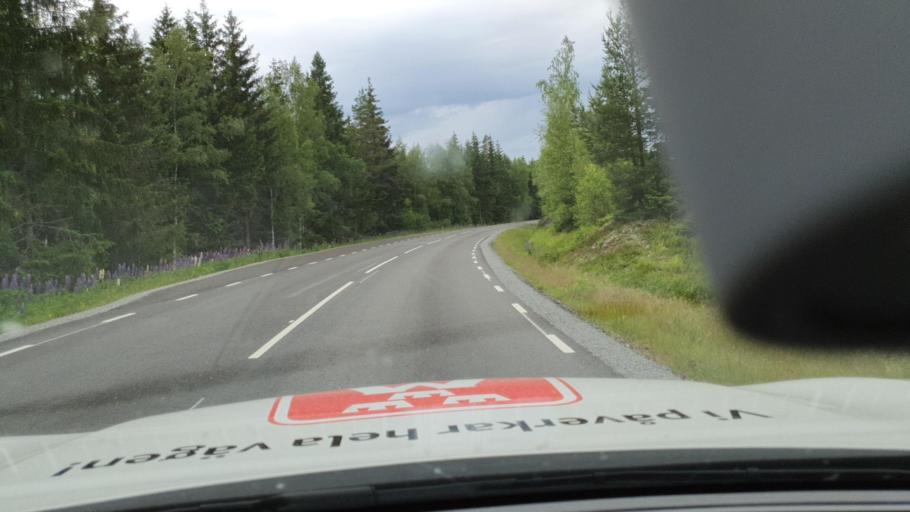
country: SE
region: OErebro
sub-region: Laxa Kommun
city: Laxa
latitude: 58.8744
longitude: 14.5097
